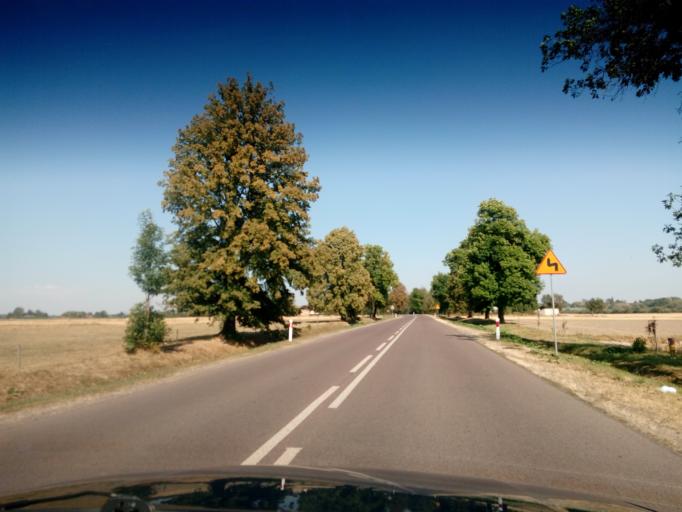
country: PL
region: Lublin Voivodeship
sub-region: Powiat hrubieszowski
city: Horodlo
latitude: 50.8526
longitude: 24.1219
